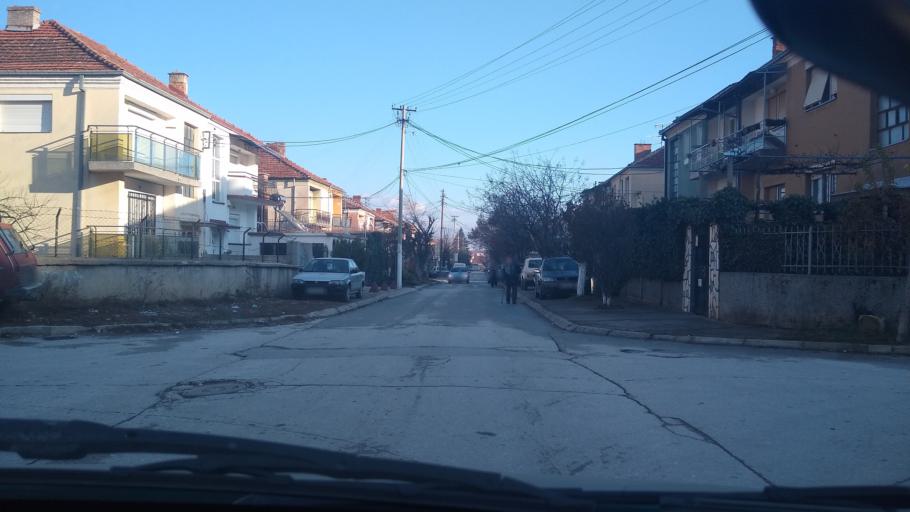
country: MK
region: Bitola
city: Bitola
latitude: 41.0301
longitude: 21.3158
